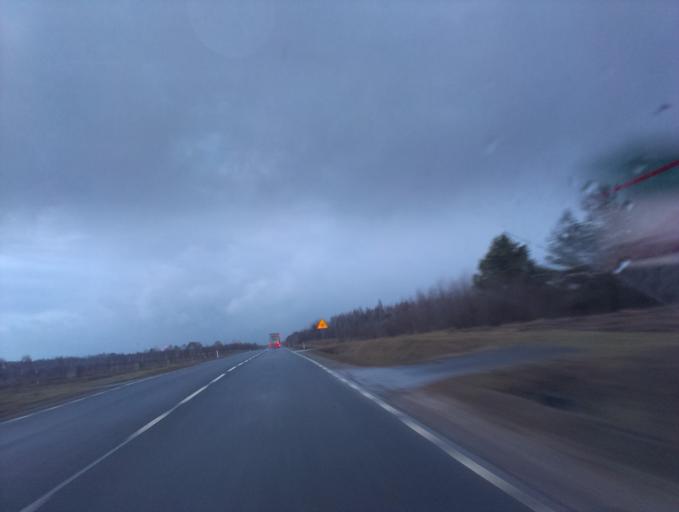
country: PL
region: Lodz Voivodeship
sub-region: Powiat opoczynski
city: Zarnow
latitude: 51.2165
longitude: 20.1916
